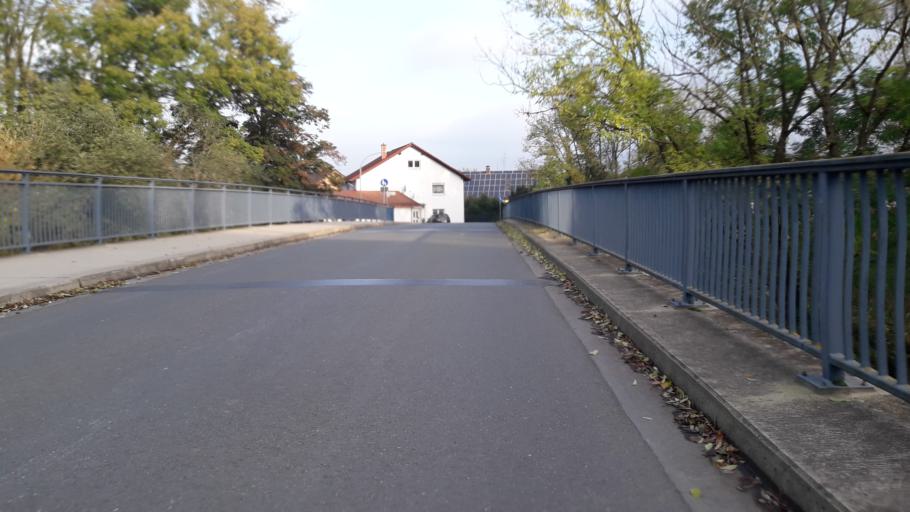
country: DE
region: North Rhine-Westphalia
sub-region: Regierungsbezirk Detmold
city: Paderborn
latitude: 51.6717
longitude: 8.7171
